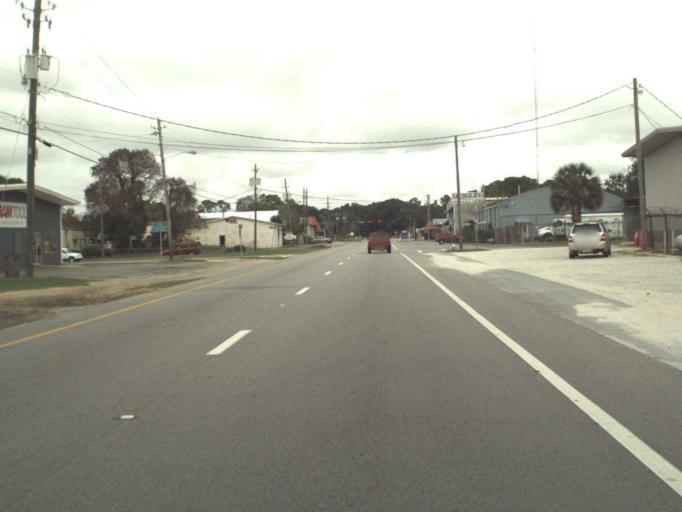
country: US
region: Florida
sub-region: Escambia County
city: Goulding
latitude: 30.4444
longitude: -87.2151
